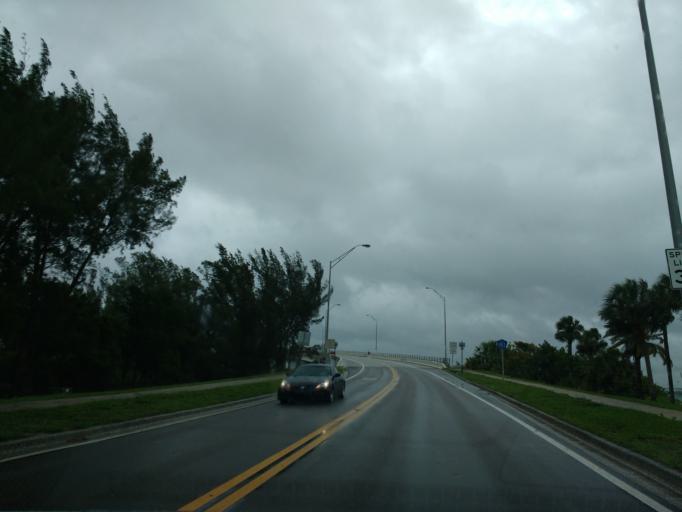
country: US
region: Florida
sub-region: Pinellas County
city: Clearwater
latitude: 27.9581
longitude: -82.8244
